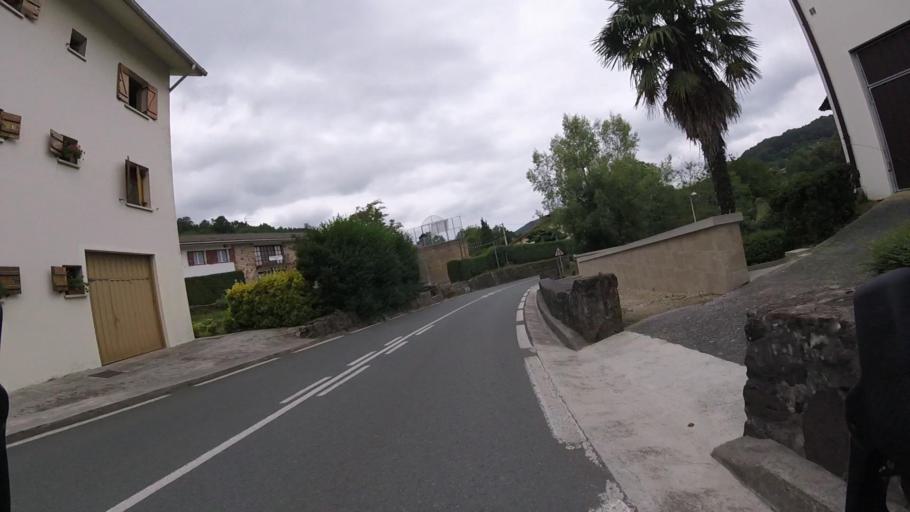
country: ES
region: Basque Country
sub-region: Provincia de Guipuzcoa
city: Lezo
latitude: 43.2882
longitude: -1.8377
